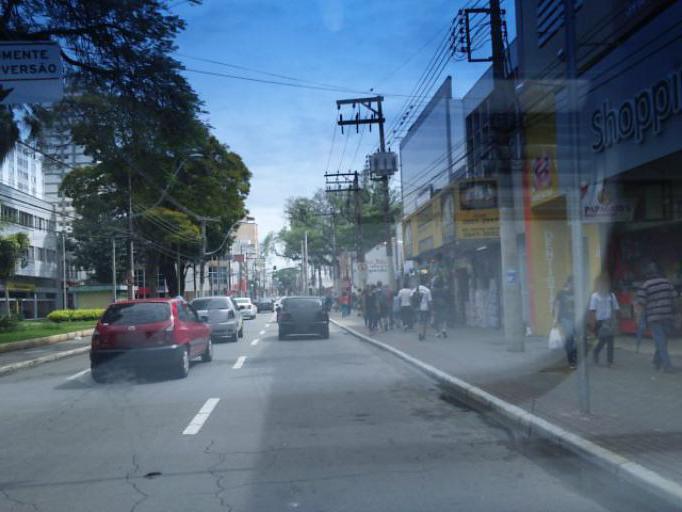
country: BR
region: Sao Paulo
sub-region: Sao Jose Dos Campos
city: Sao Jose dos Campos
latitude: -23.1838
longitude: -45.8868
